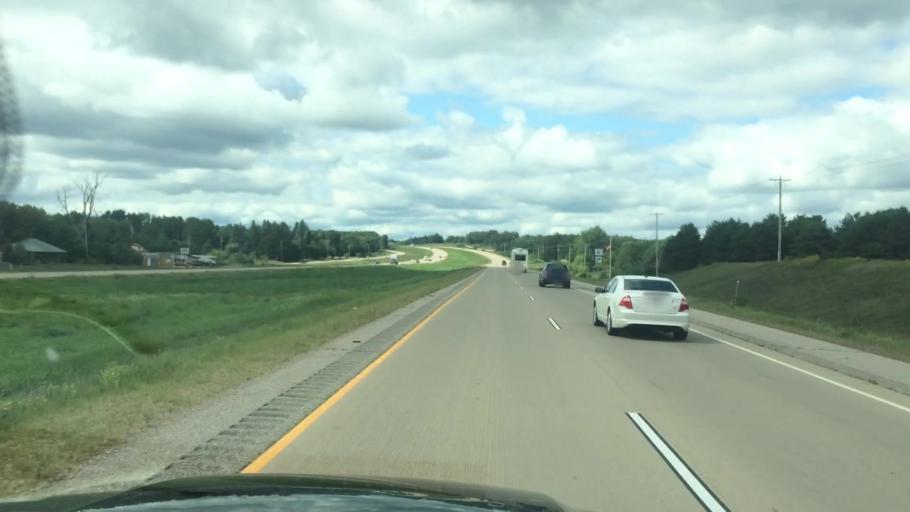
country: US
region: Wisconsin
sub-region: Portage County
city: Plover
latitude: 44.5104
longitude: -89.4223
